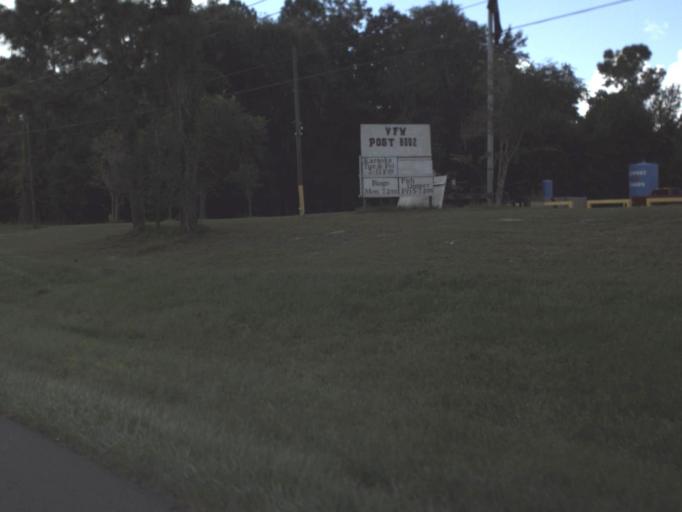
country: US
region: Florida
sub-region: Polk County
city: Gibsonia
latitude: 28.1698
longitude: -81.9799
